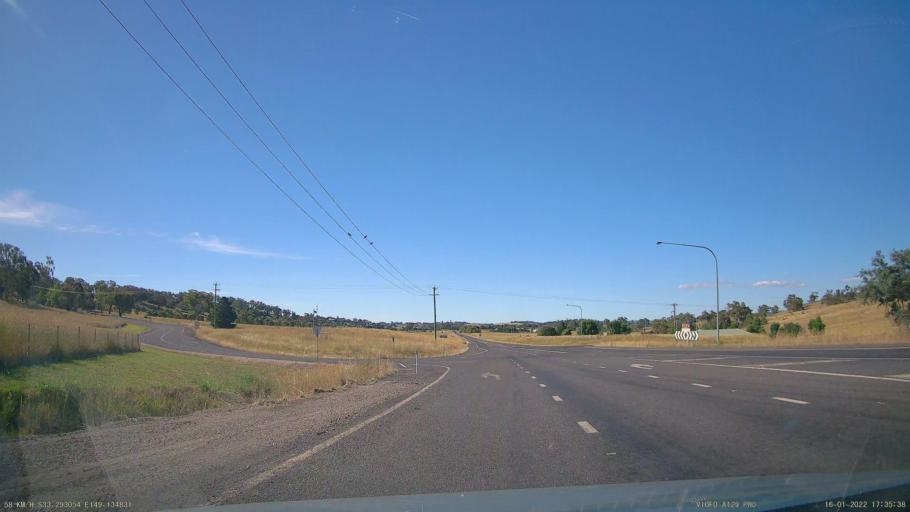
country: AU
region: New South Wales
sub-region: Orange Municipality
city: Orange
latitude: -33.2929
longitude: 149.1349
